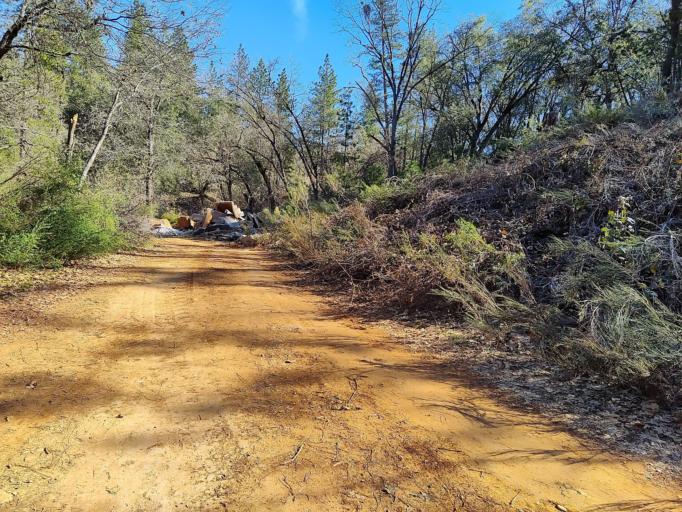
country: US
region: California
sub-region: Placer County
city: Meadow Vista
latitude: 39.0335
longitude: -120.9797
